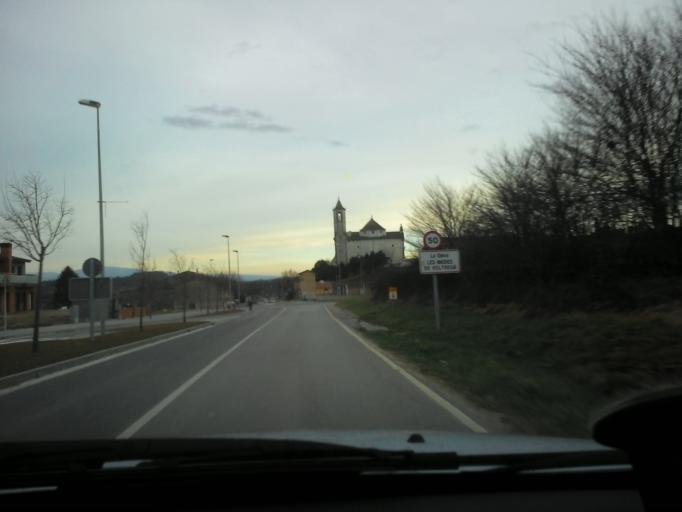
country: ES
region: Catalonia
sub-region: Provincia de Barcelona
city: Santa Cecilia de Voltrega
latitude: 42.0065
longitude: 2.2410
